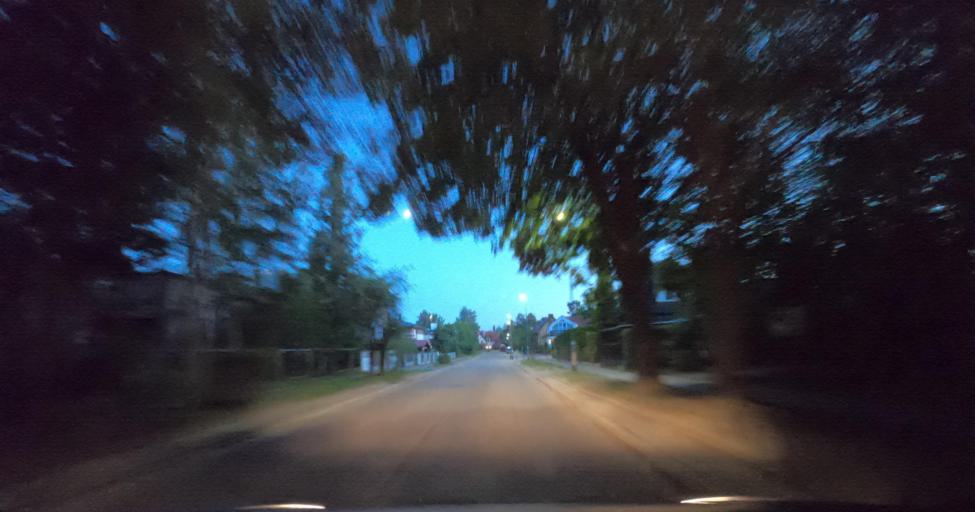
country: PL
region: Pomeranian Voivodeship
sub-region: Gdynia
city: Wielki Kack
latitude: 54.4281
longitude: 18.4673
